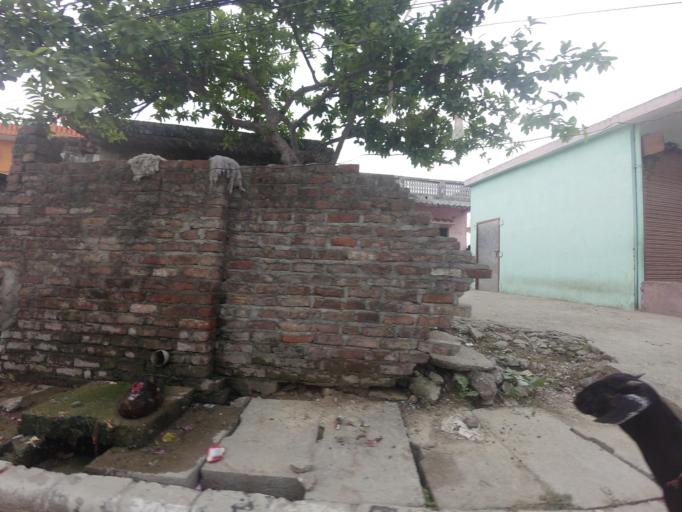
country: NP
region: Western Region
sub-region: Lumbini Zone
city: Bhairahawa
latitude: 27.5099
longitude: 83.4243
